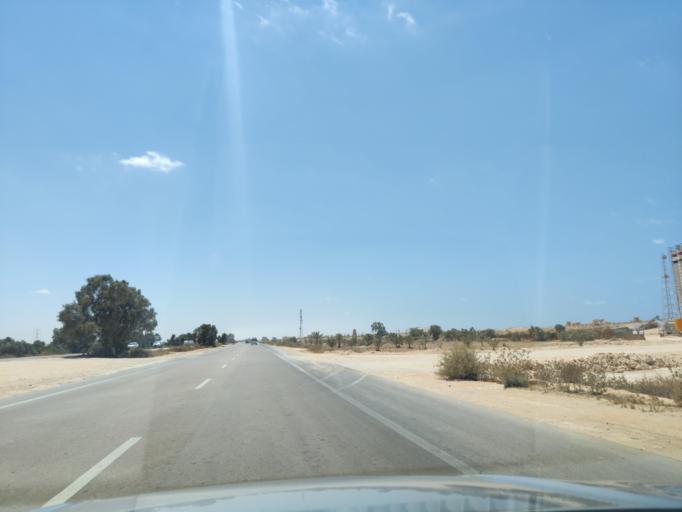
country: EG
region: Muhafazat Matruh
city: Al `Alamayn
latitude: 31.0699
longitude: 28.1439
